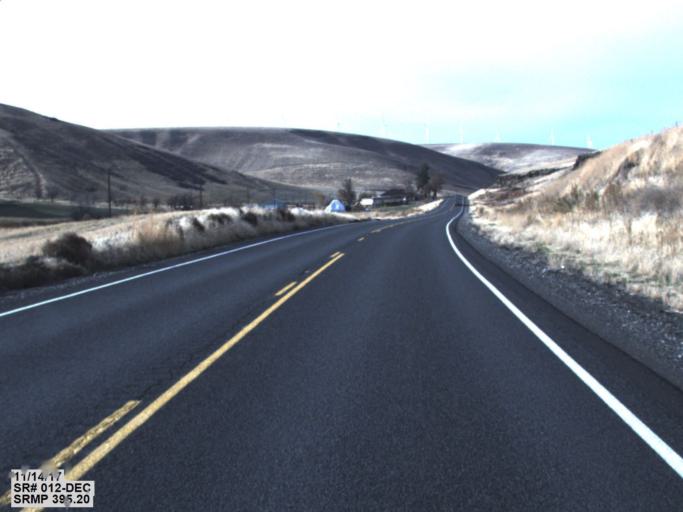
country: US
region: Washington
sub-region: Garfield County
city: Pomeroy
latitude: 46.4872
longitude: -117.7551
